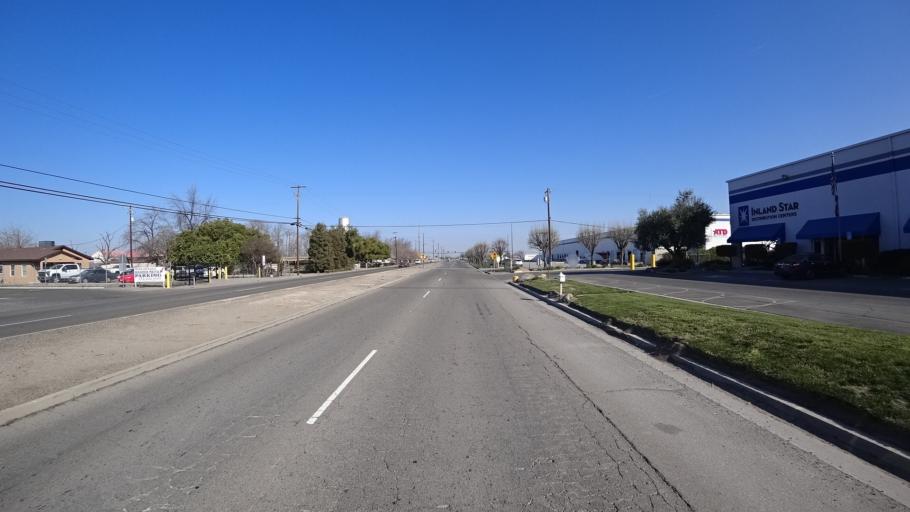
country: US
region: California
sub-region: Fresno County
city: Easton
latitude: 36.6903
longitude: -119.7365
